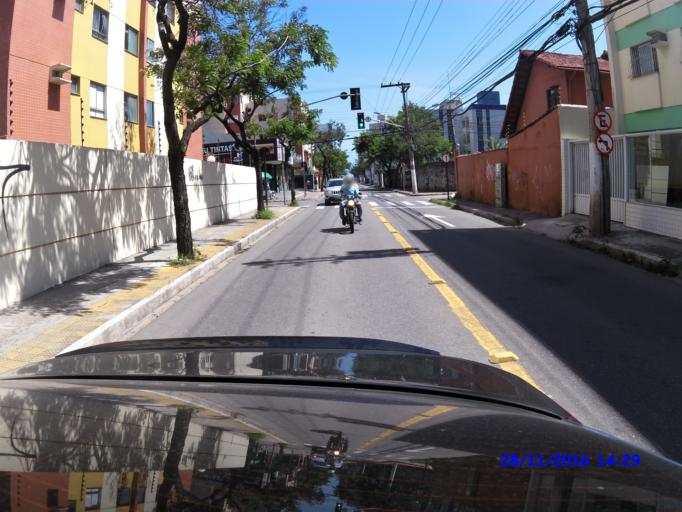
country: BR
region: Espirito Santo
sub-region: Vila Velha
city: Vila Velha
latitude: -20.2609
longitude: -40.2637
